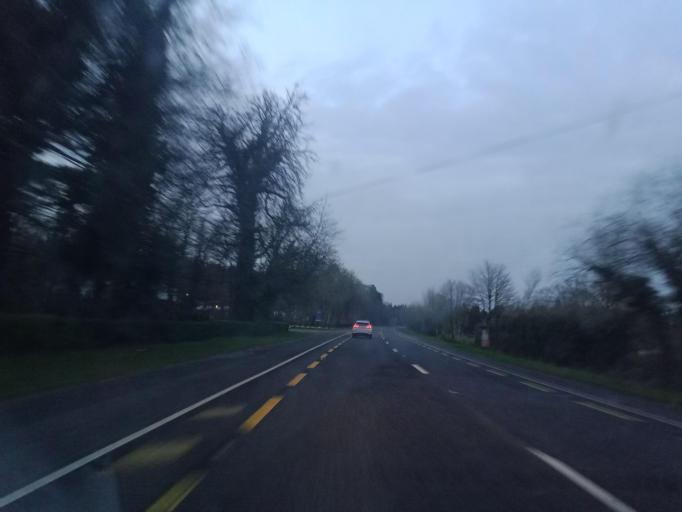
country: IE
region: Leinster
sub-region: Laois
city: Abbeyleix
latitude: 52.8860
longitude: -7.3647
